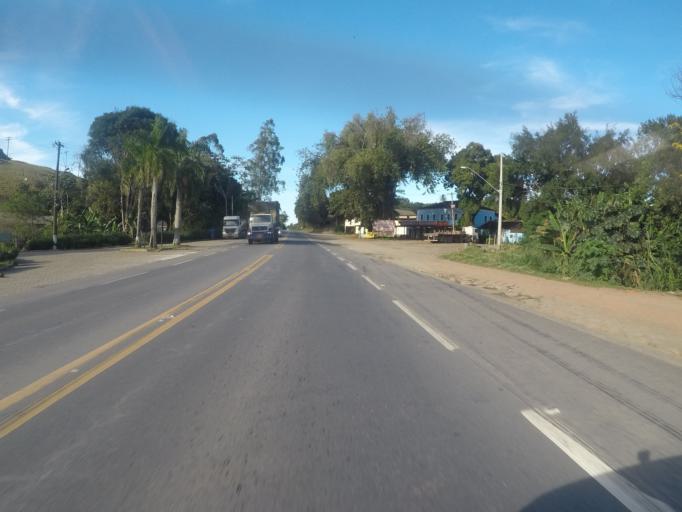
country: BR
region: Espirito Santo
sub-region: Ibiracu
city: Ibiracu
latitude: -19.8682
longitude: -40.4058
